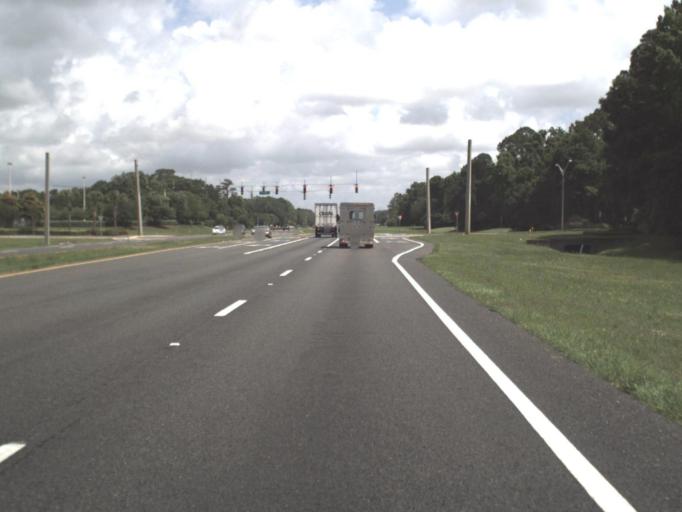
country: US
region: Florida
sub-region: Saint Johns County
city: Fruit Cove
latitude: 30.1839
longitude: -81.5516
